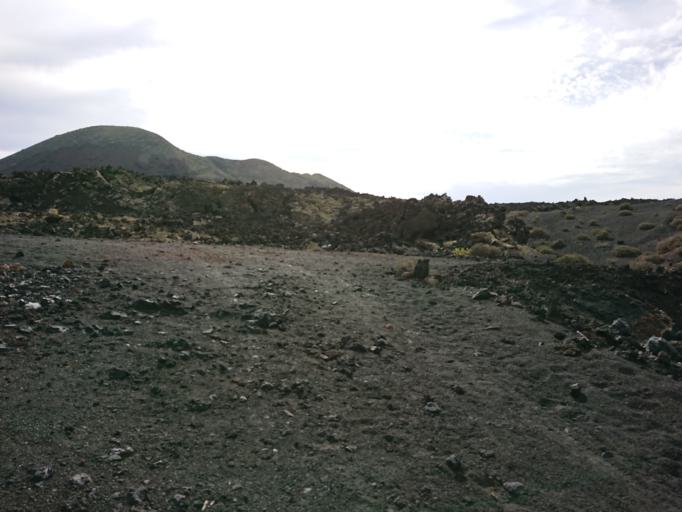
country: ES
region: Canary Islands
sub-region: Provincia de Las Palmas
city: Tinajo
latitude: 29.0127
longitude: -13.6775
